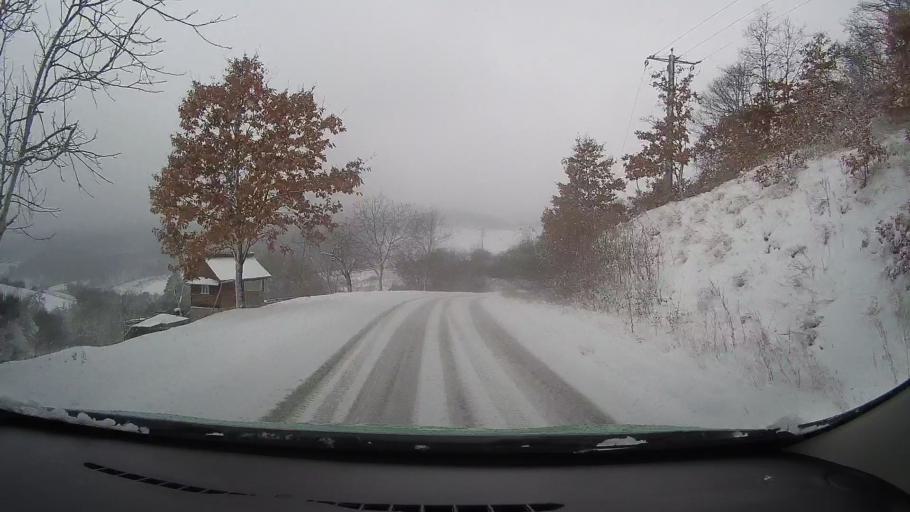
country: RO
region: Hunedoara
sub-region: Comuna Carjiti
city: Carjiti
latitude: 45.8396
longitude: 22.8418
